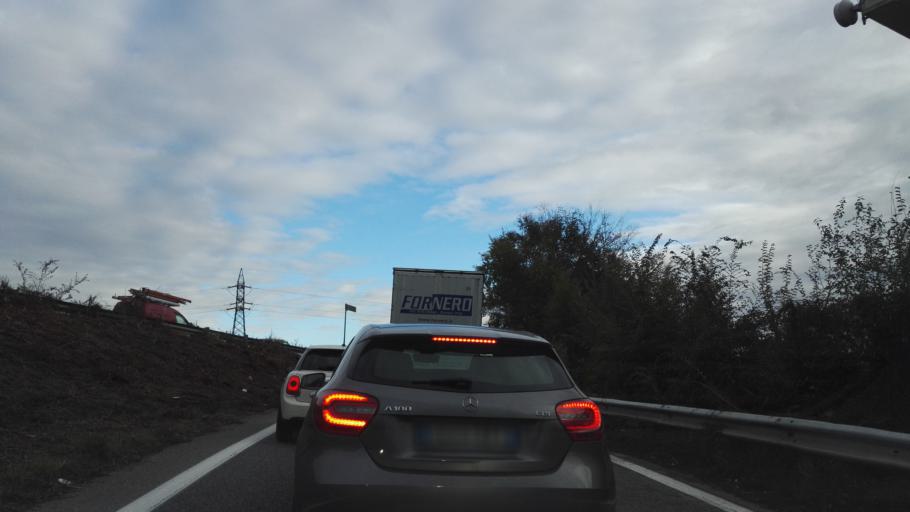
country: IT
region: Lombardy
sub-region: Provincia di Bergamo
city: Bergamo
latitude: 45.6777
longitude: 9.6714
